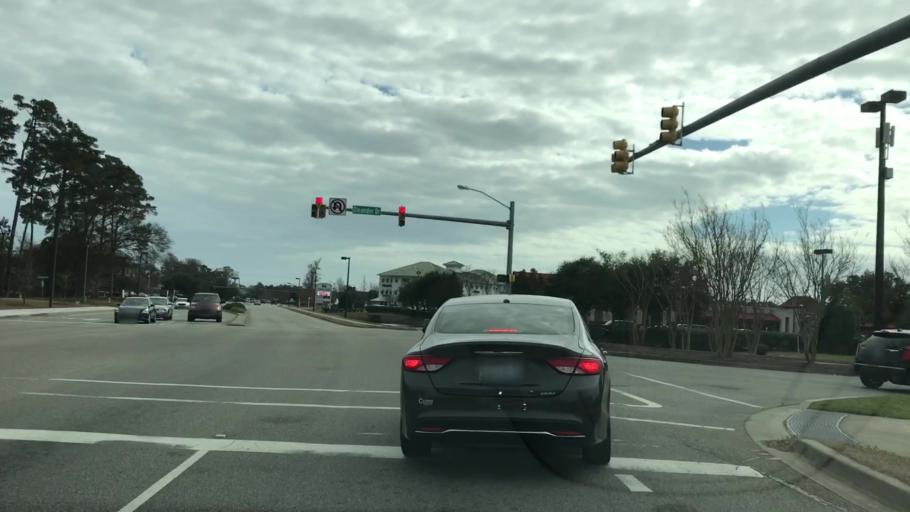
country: US
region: South Carolina
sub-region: Horry County
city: Myrtle Beach
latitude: 33.7267
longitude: -78.8688
